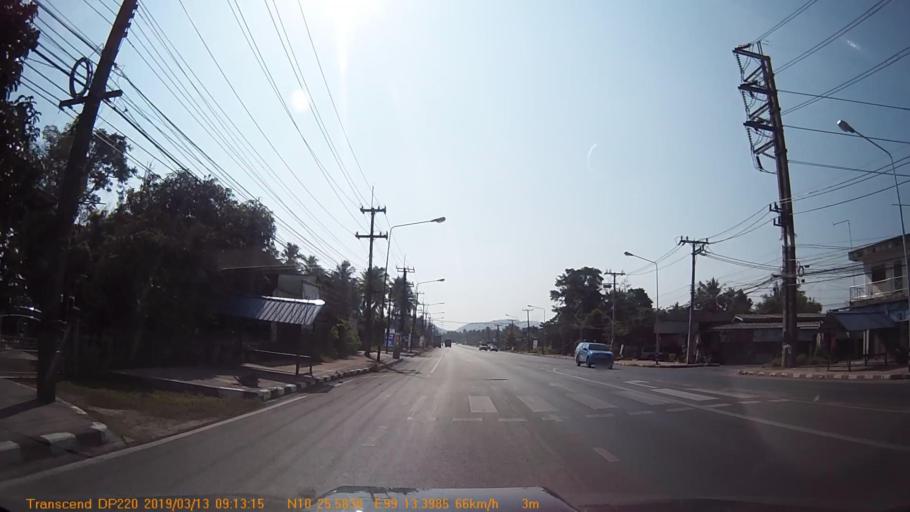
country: TH
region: Chumphon
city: Chumphon
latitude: 10.4267
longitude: 99.2232
